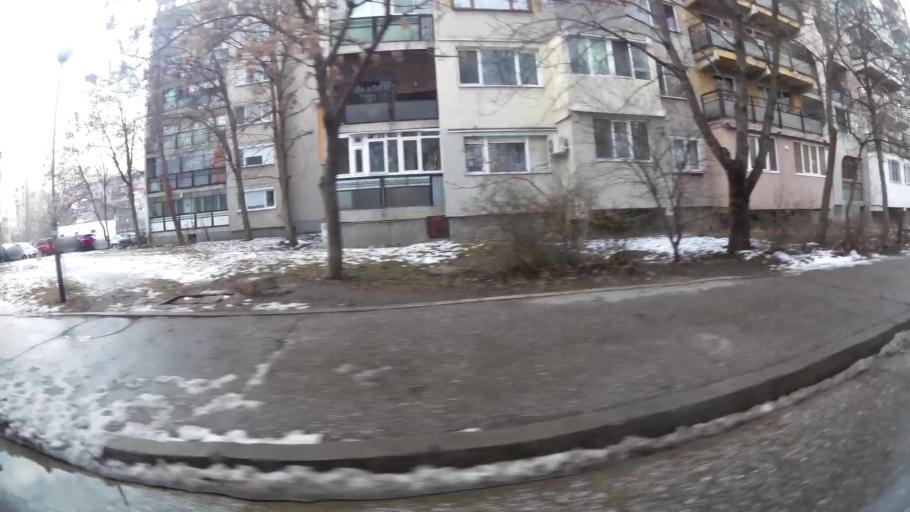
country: BG
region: Sofia-Capital
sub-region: Stolichna Obshtina
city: Sofia
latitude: 42.6996
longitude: 23.2847
